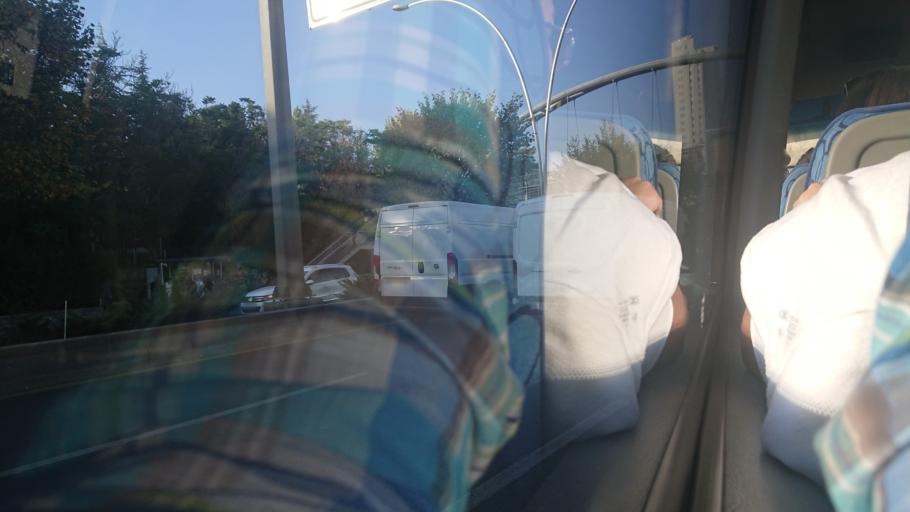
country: TR
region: Ankara
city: Ankara
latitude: 39.9351
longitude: 32.8224
